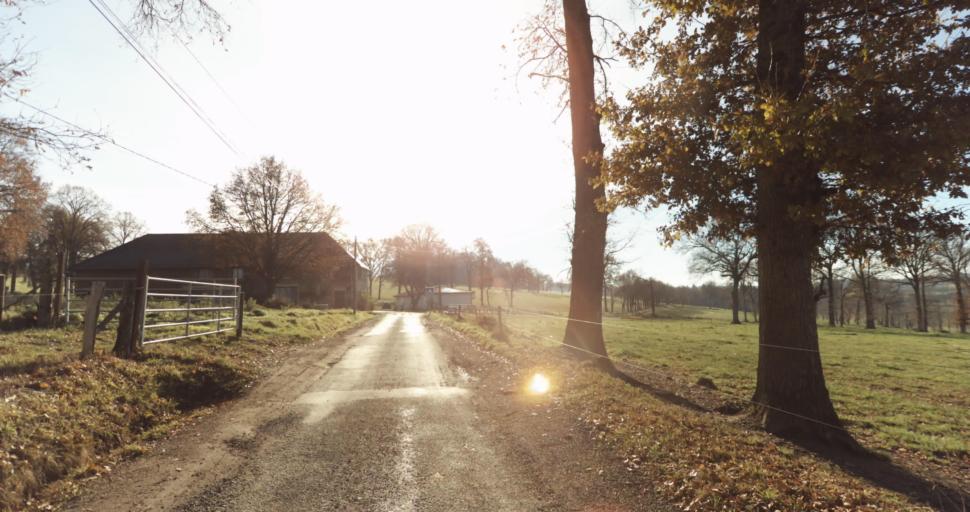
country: FR
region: Limousin
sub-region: Departement de la Haute-Vienne
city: Aixe-sur-Vienne
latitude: 45.7832
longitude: 1.1162
